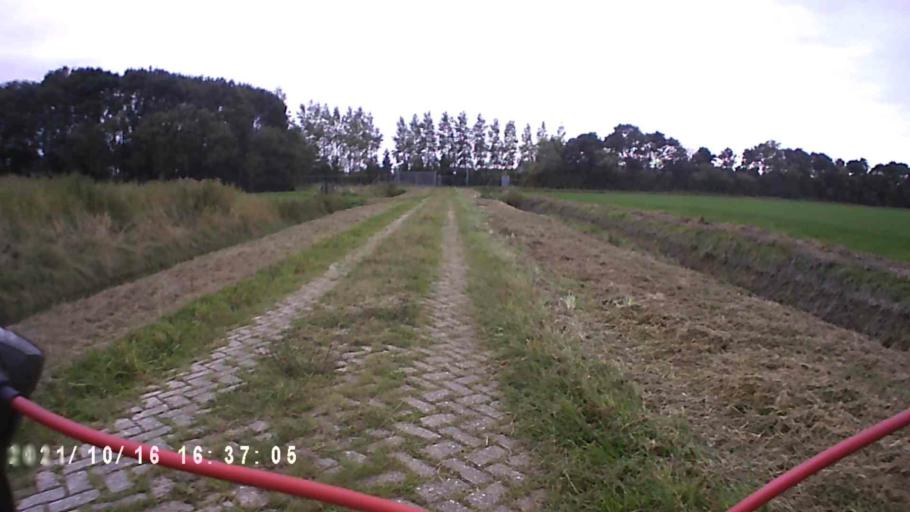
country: NL
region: Friesland
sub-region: Gemeente Dongeradeel
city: Anjum
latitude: 53.3742
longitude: 6.1516
